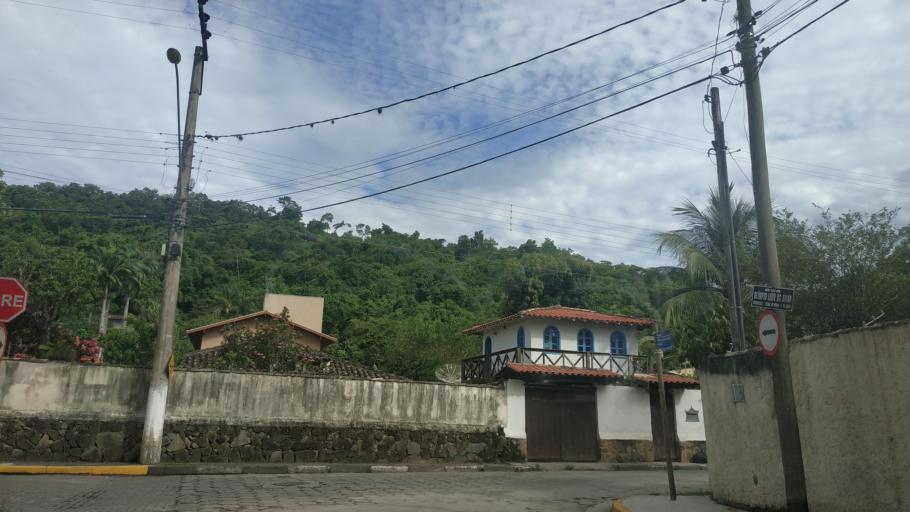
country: BR
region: Sao Paulo
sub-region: Ilhabela
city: Ilhabela
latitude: -23.8145
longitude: -45.3640
